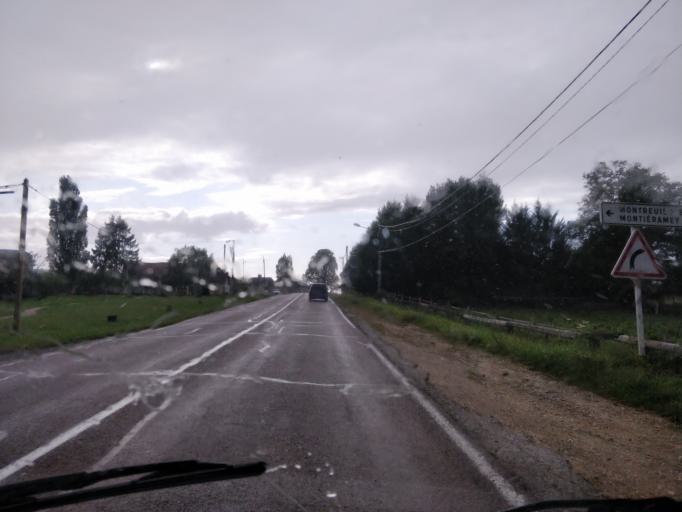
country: FR
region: Champagne-Ardenne
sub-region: Departement de l'Aube
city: Lusigny-sur-Barse
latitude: 48.2395
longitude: 4.3006
